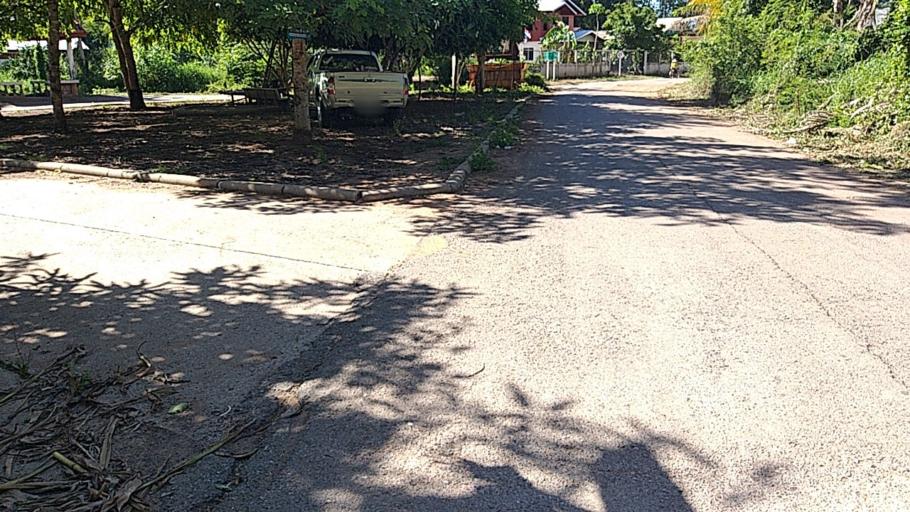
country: TH
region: Chaiyaphum
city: Ban Thaen
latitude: 16.4052
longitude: 102.3525
